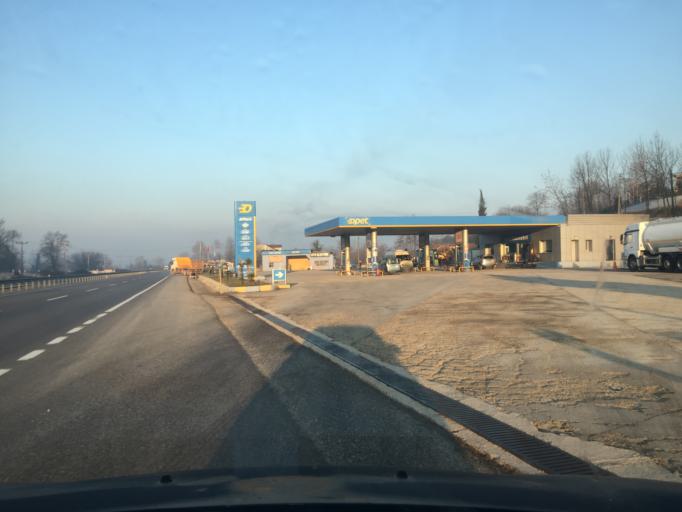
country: TR
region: Sakarya
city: Akyazi
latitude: 40.6313
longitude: 30.6369
